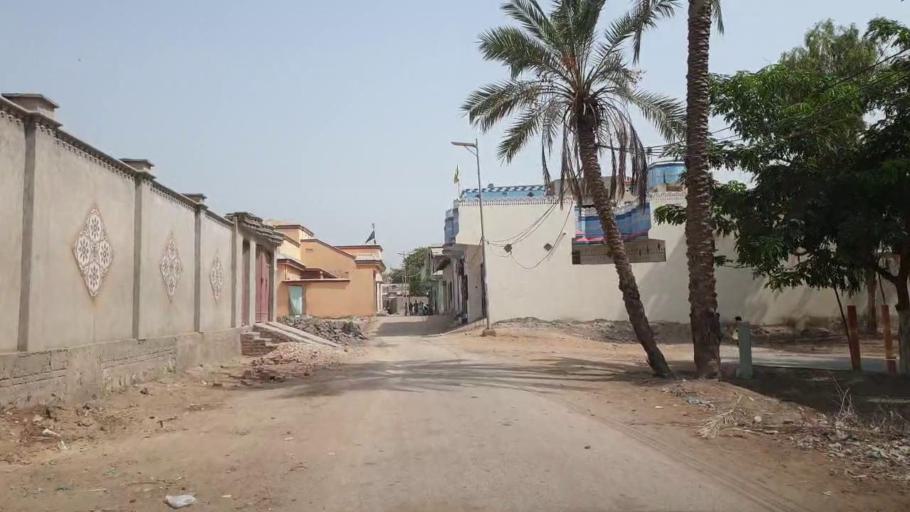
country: PK
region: Sindh
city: Gambat
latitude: 27.3771
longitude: 68.5156
